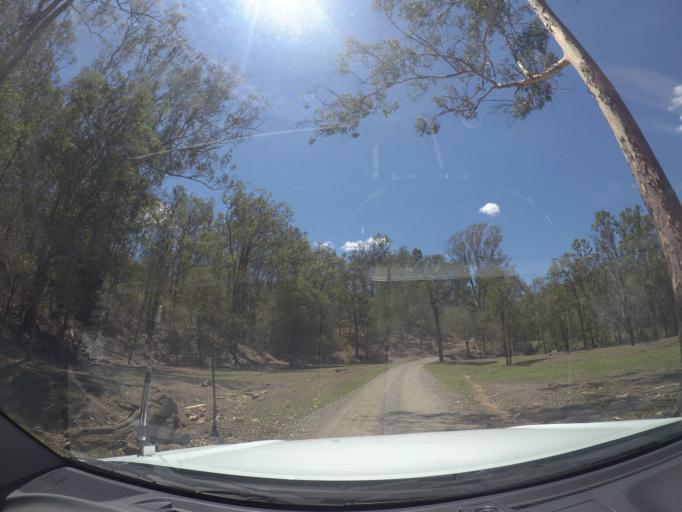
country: AU
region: Queensland
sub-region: Ipswich
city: Deebing Heights
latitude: -27.7621
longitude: 152.8076
